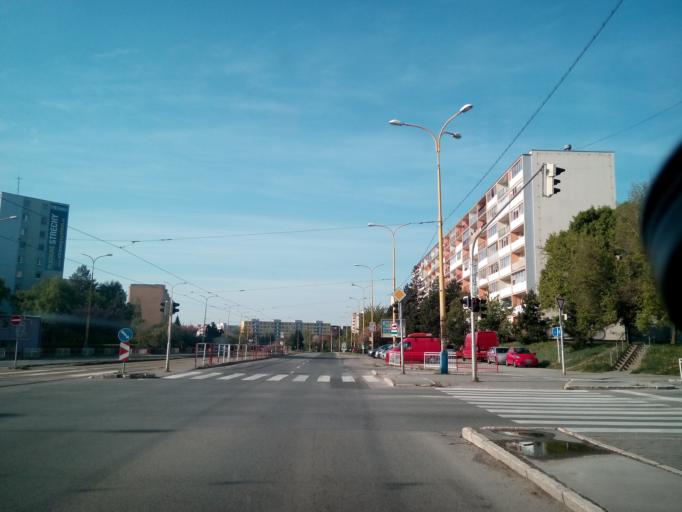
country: SK
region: Kosicky
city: Kosice
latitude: 48.7223
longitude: 21.2350
